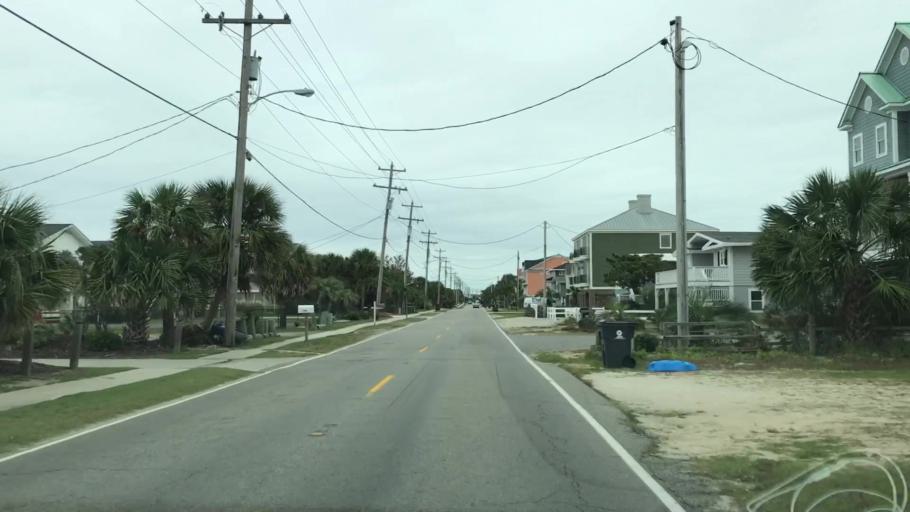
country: US
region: South Carolina
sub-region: Georgetown County
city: Murrells Inlet
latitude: 33.5585
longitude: -79.0142
